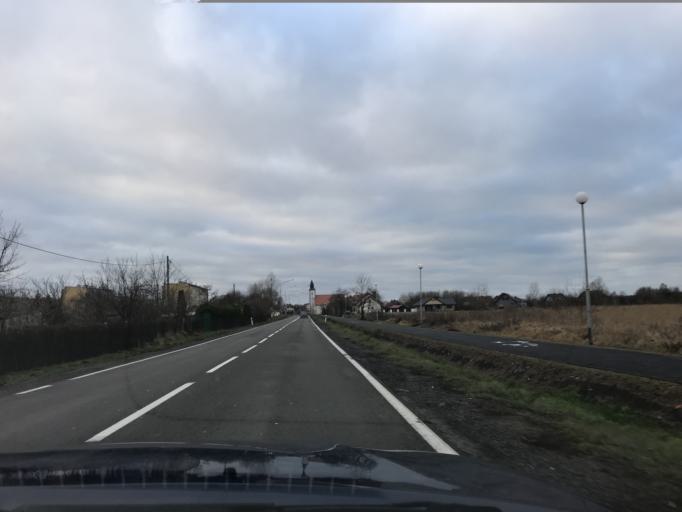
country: PL
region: West Pomeranian Voivodeship
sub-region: Powiat drawski
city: Zlocieniec
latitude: 53.5345
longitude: 16.0293
